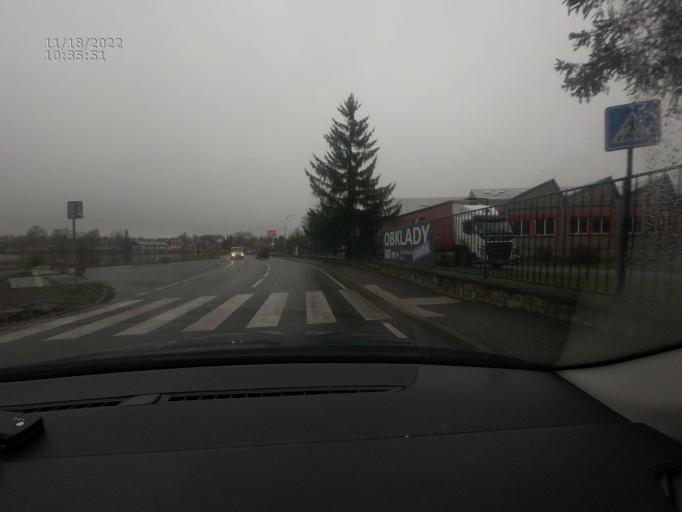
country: CZ
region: Central Bohemia
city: Zebrak
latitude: 49.8715
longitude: 13.8943
